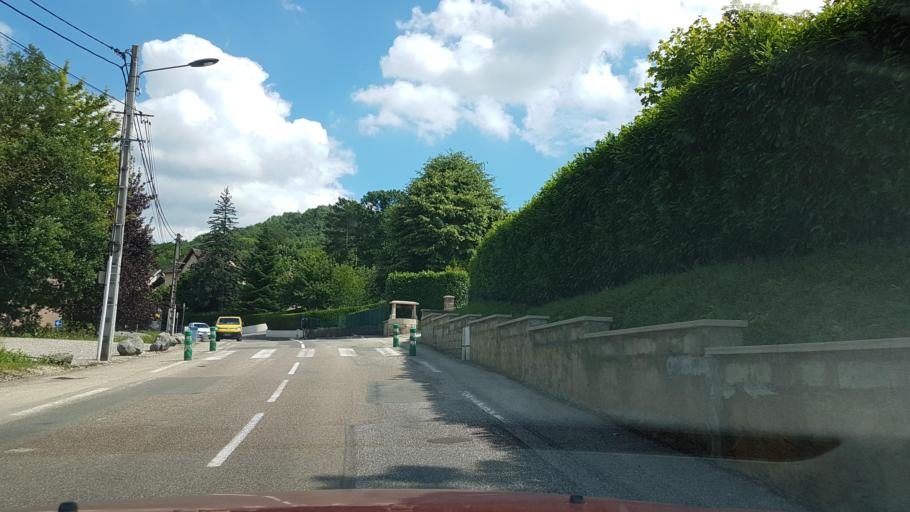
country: FR
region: Franche-Comte
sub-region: Departement du Jura
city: Lons-le-Saunier
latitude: 46.6658
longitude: 5.5652
